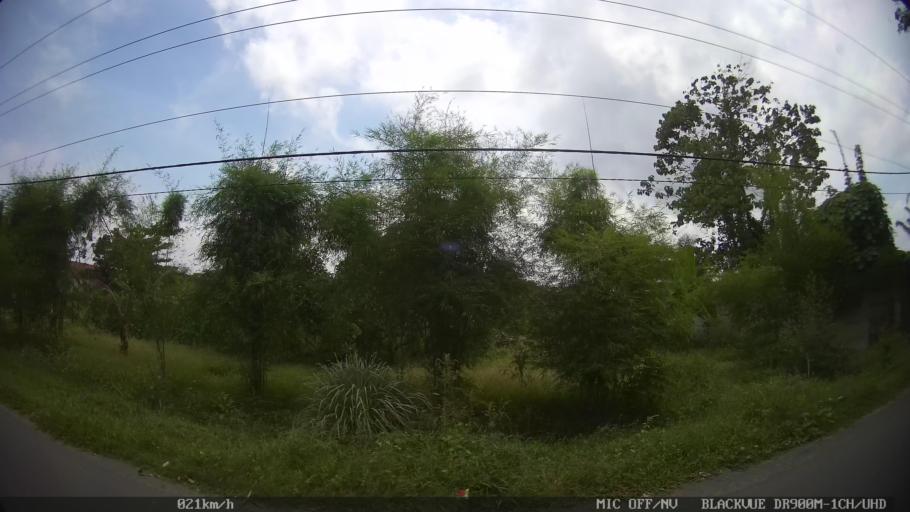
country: ID
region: North Sumatra
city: Labuhan Deli
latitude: 3.7097
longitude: 98.6653
